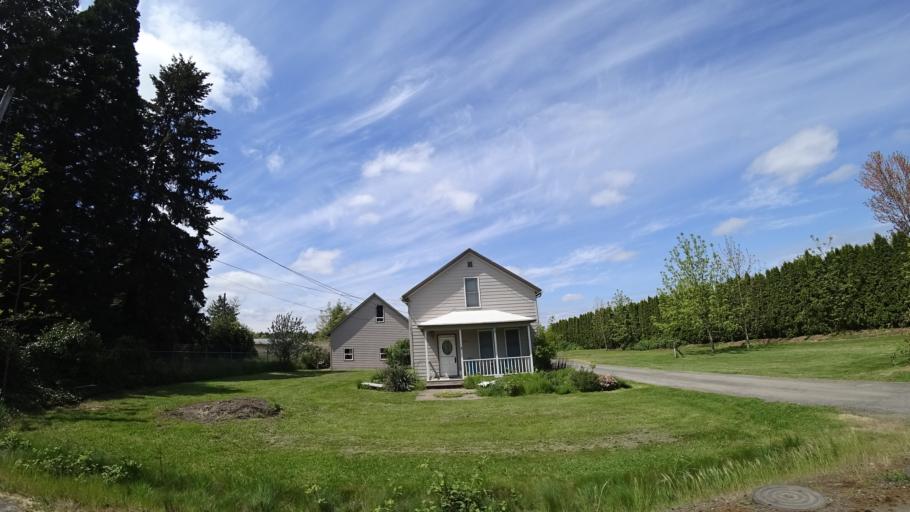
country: US
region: Oregon
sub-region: Washington County
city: Aloha
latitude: 45.4784
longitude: -122.8943
